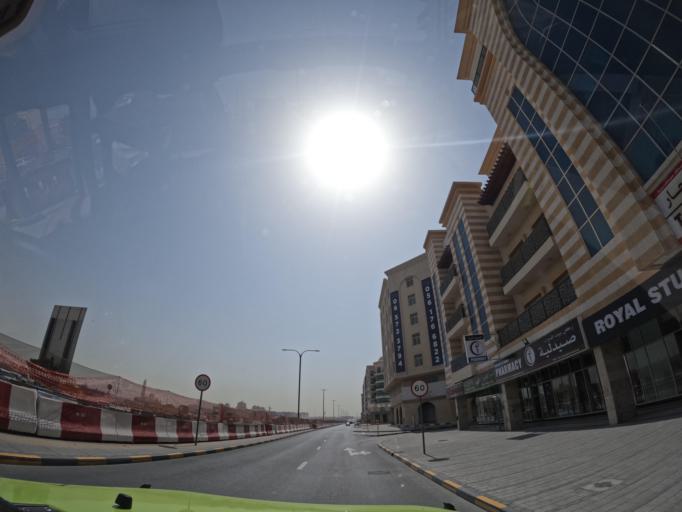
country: AE
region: Ash Shariqah
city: Sharjah
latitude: 25.3087
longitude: 55.4618
